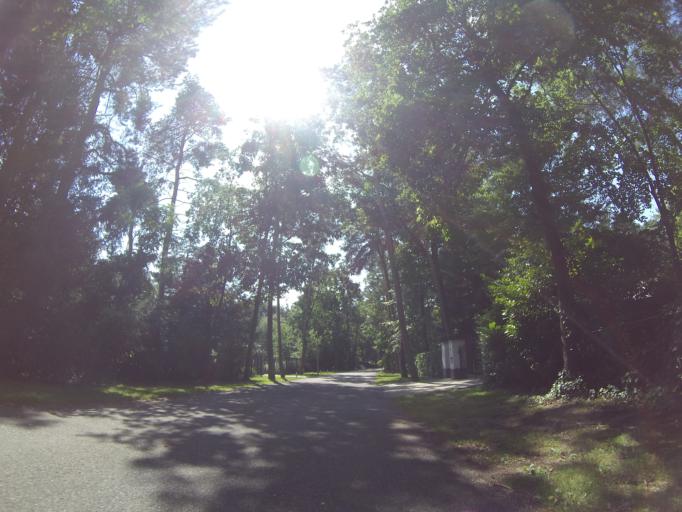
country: NL
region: Utrecht
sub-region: Gemeente Zeist
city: Zeist
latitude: 52.1117
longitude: 5.2405
